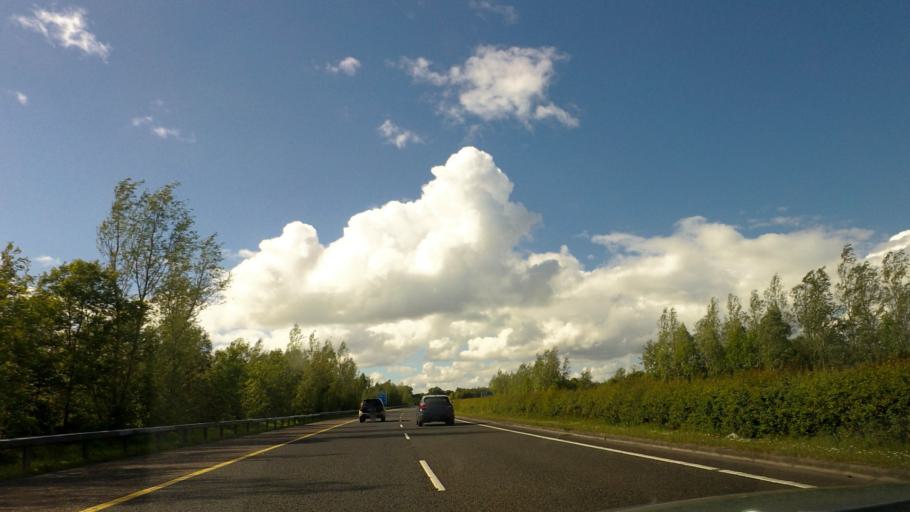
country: IE
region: Munster
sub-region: An Clar
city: Newmarket on Fergus
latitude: 52.7313
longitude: -8.8857
